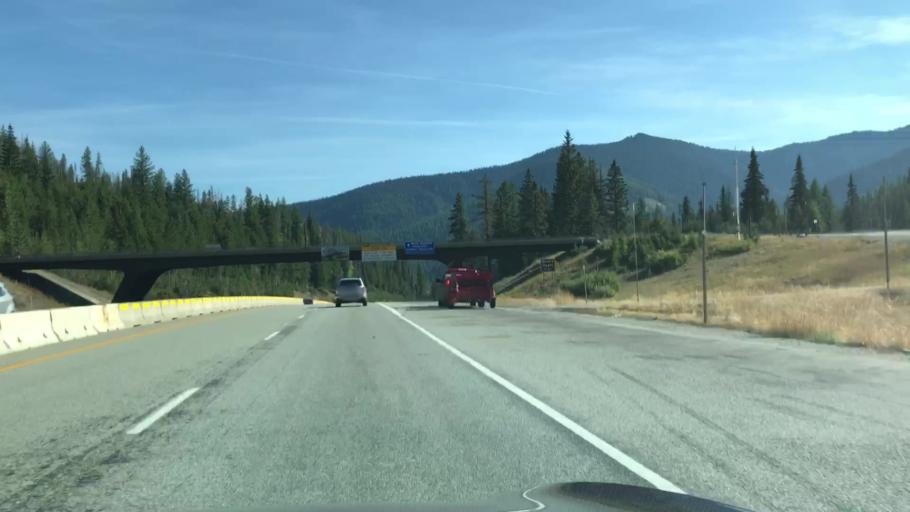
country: US
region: Idaho
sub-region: Shoshone County
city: Wallace
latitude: 47.4544
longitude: -115.6948
